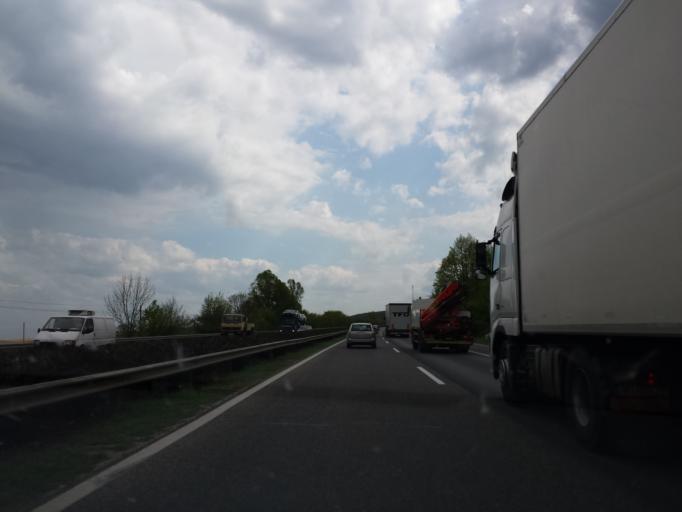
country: HU
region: Fejer
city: Szarliget
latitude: 47.5436
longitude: 18.4980
